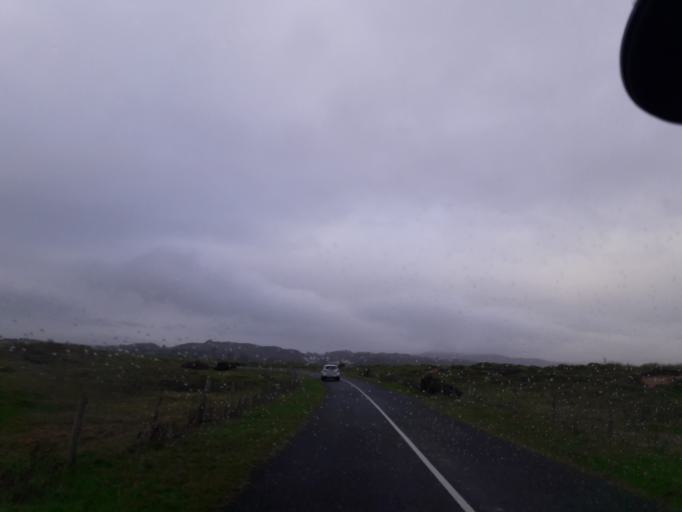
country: IE
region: Ulster
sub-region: County Donegal
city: Ramelton
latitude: 55.1888
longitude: -7.6114
